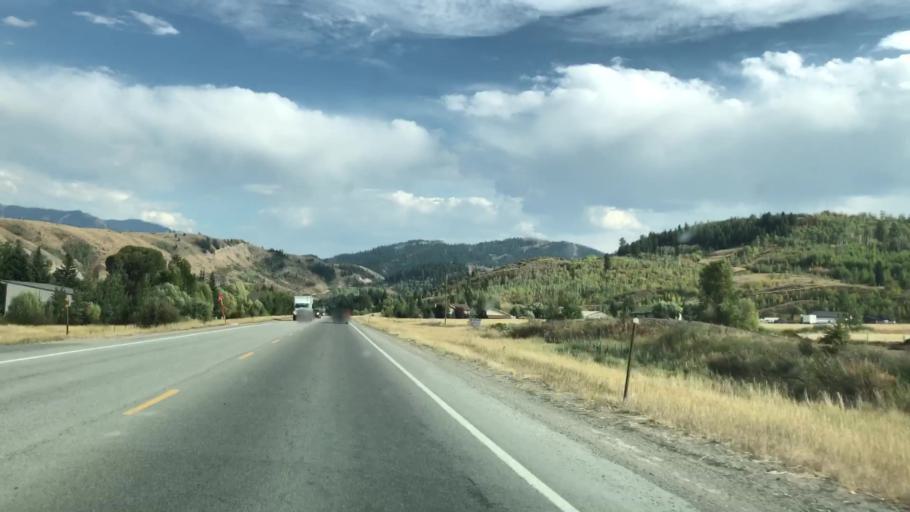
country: US
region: Wyoming
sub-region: Teton County
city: South Park
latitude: 43.3667
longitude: -110.7337
